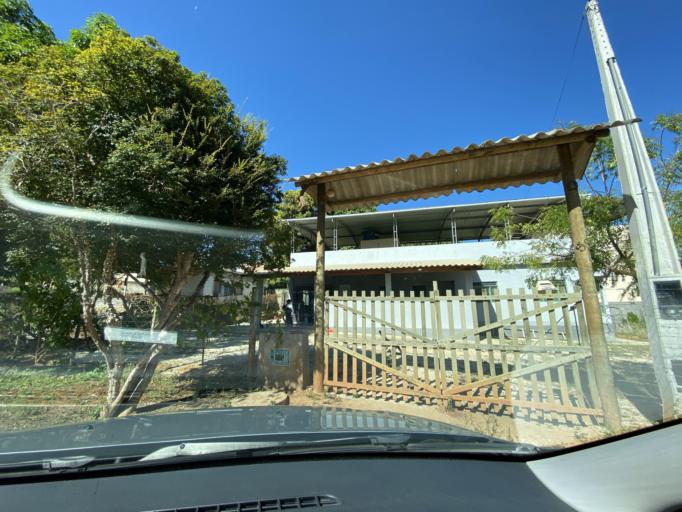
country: BR
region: Espirito Santo
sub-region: Jeronimo Monteiro
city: Jeronimo Monteiro
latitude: -20.7954
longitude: -41.4012
